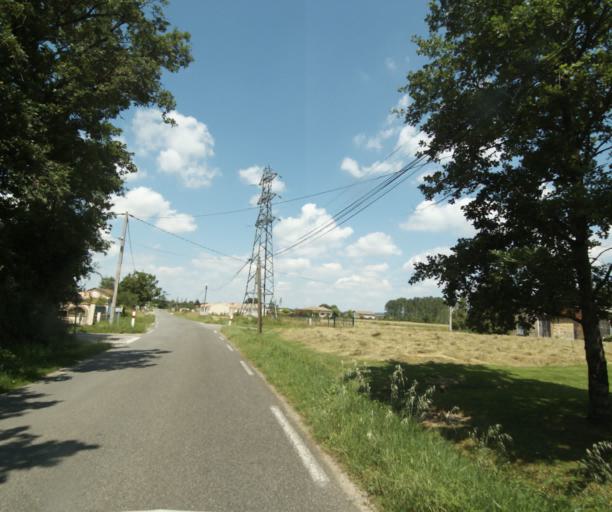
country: FR
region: Midi-Pyrenees
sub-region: Departement du Tarn-et-Garonne
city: Montauban
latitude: 44.0550
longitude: 1.3410
